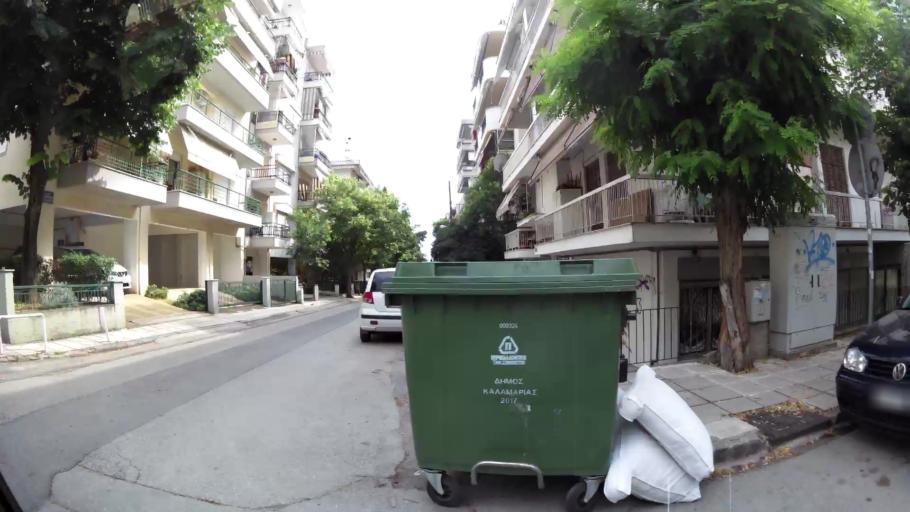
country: GR
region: Central Macedonia
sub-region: Nomos Thessalonikis
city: Kalamaria
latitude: 40.5792
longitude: 22.9506
